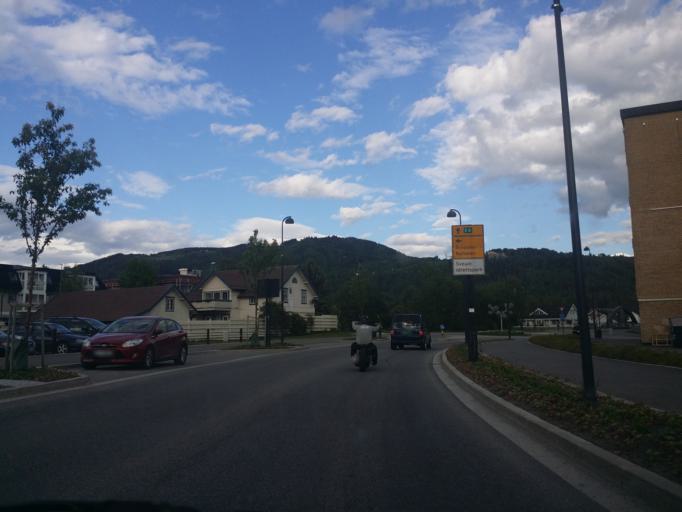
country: NO
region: Hedmark
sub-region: Ringsaker
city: Brumunddal
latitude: 60.8863
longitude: 10.9386
